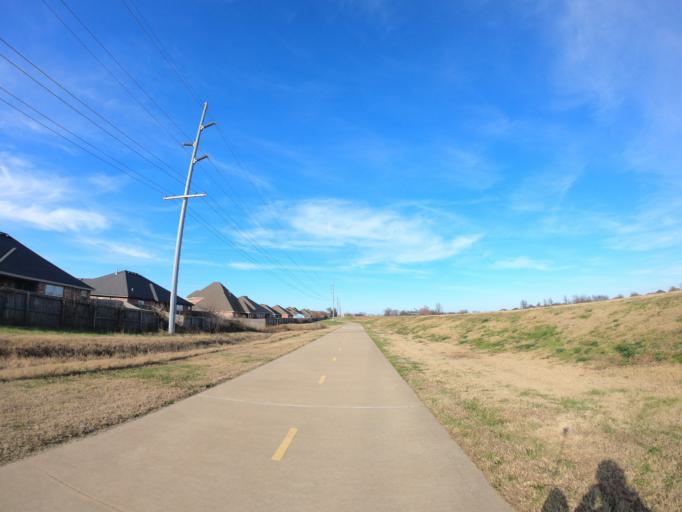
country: US
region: Arkansas
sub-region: Benton County
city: Lowell
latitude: 36.2699
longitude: -94.1676
